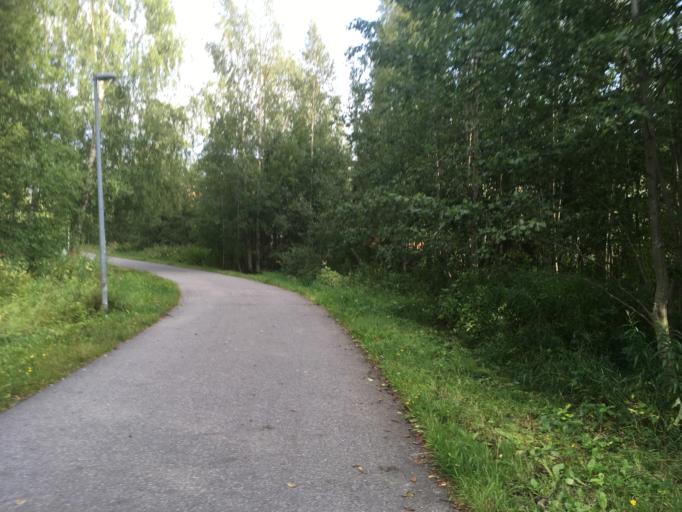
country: FI
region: Central Finland
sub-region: Jyvaeskylae
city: Jyvaeskylae
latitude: 62.2260
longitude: 25.7879
